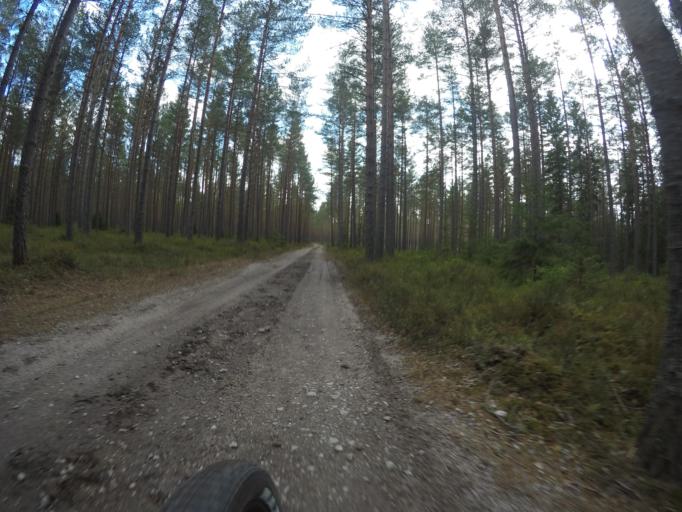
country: SE
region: Vaestmanland
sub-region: Kungsors Kommun
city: Kungsoer
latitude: 59.3630
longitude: 16.1080
